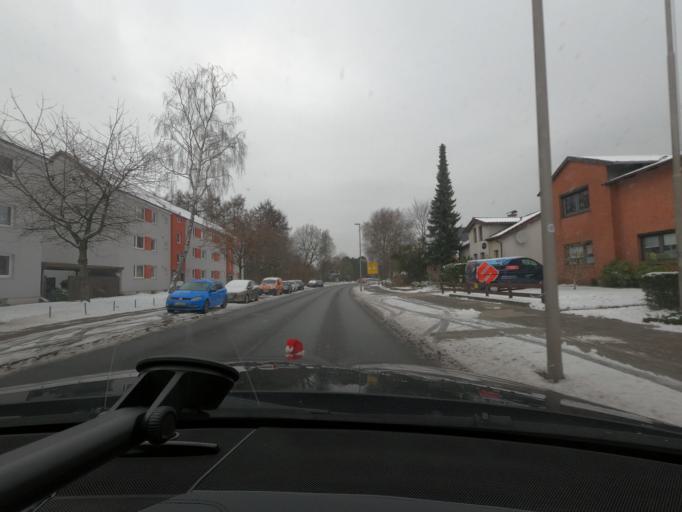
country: DE
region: Schleswig-Holstein
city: Jarplund-Weding
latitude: 54.7631
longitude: 9.3956
